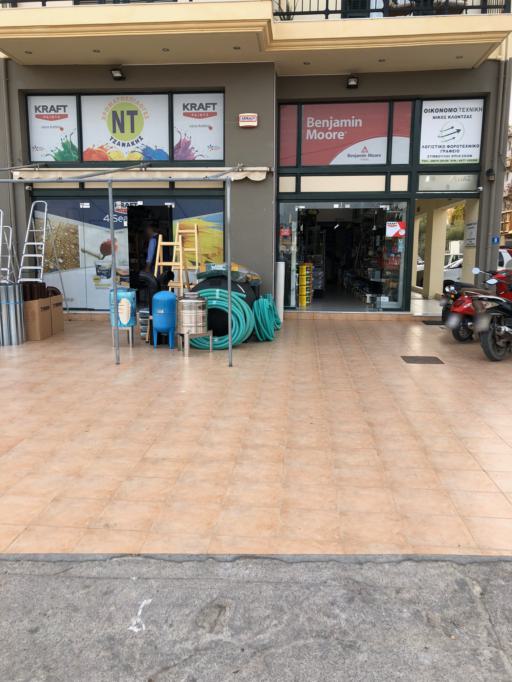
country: GR
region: Crete
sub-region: Nomos Irakleiou
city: Limin Khersonisou
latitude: 35.3192
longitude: 25.3890
